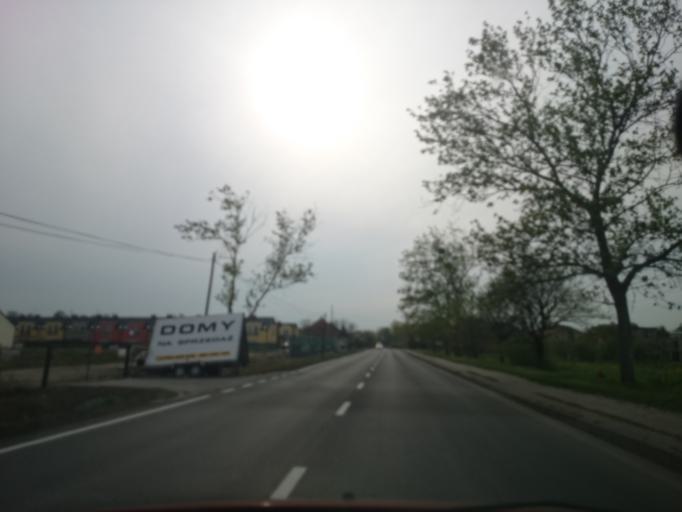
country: PL
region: Opole Voivodeship
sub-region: Powiat opolski
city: Chmielowice
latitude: 50.6818
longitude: 17.8574
